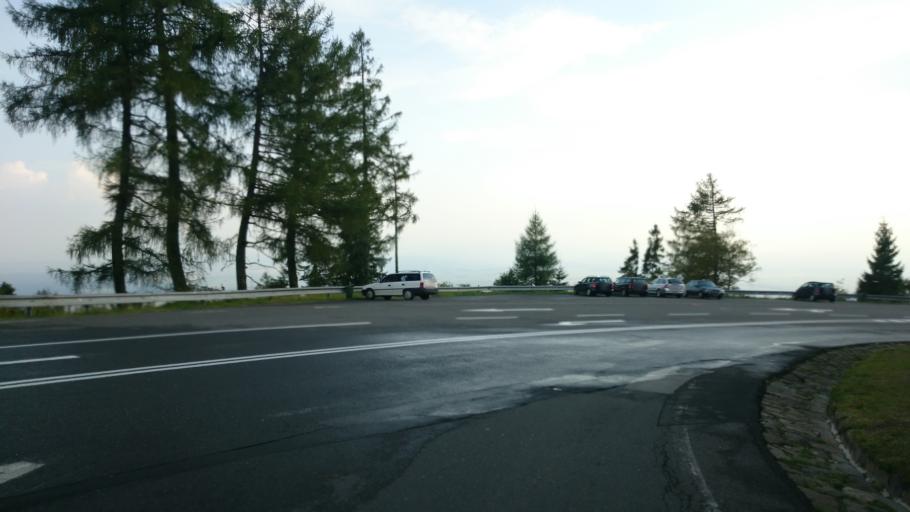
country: SK
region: Presovsky
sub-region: Okres Poprad
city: Strba
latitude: 49.1114
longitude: 20.0709
